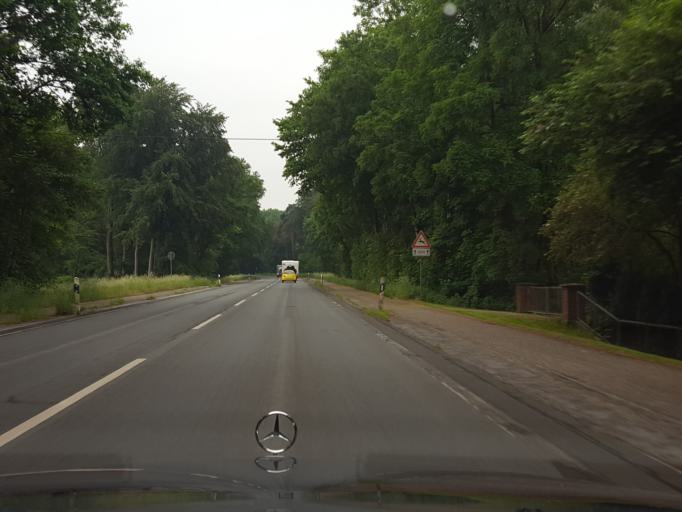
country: DE
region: North Rhine-Westphalia
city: Oer-Erkenschwick
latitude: 51.6882
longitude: 7.2970
